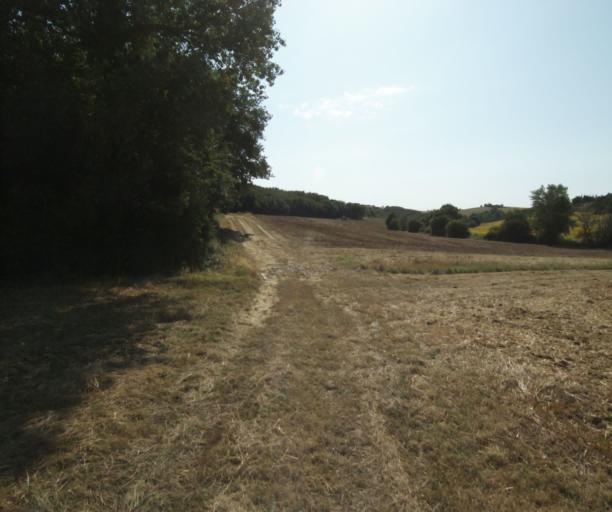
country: FR
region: Midi-Pyrenees
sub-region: Departement de la Haute-Garonne
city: Saint-Felix-Lauragais
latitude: 43.4192
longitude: 1.8355
